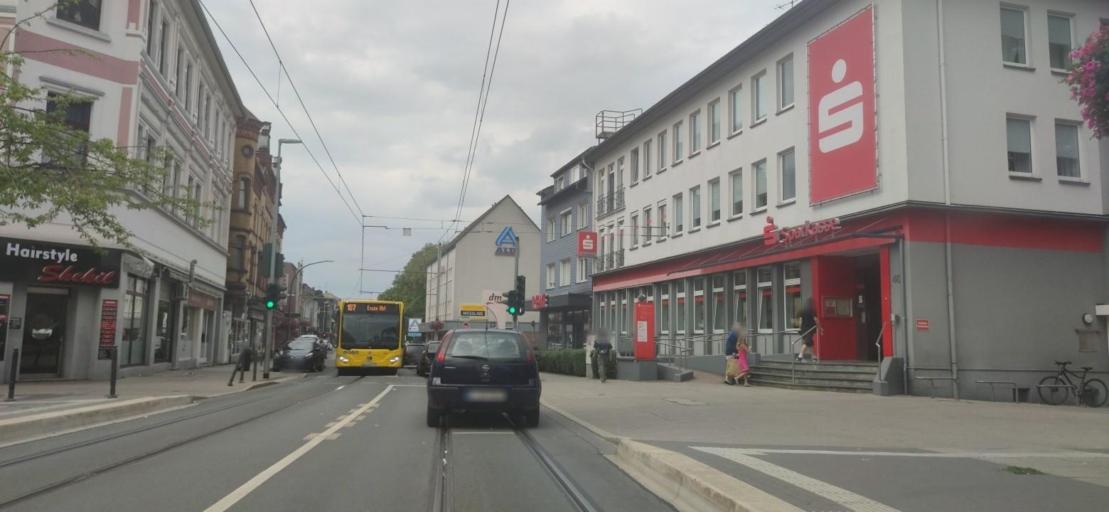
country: DE
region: North Rhine-Westphalia
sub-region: Regierungsbezirk Dusseldorf
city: Essen
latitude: 51.4972
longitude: 7.0484
